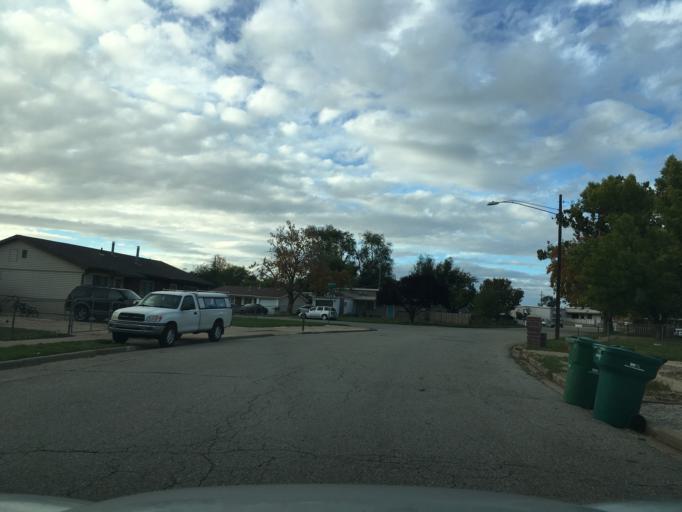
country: US
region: Utah
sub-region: Davis County
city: Layton
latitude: 41.0810
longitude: -111.9945
